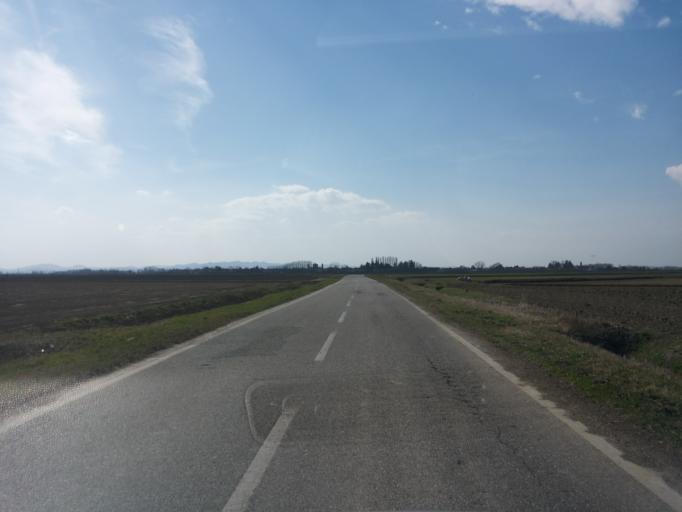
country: IT
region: Piedmont
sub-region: Provincia di Vercelli
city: Costanzana
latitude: 45.2447
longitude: 8.3848
